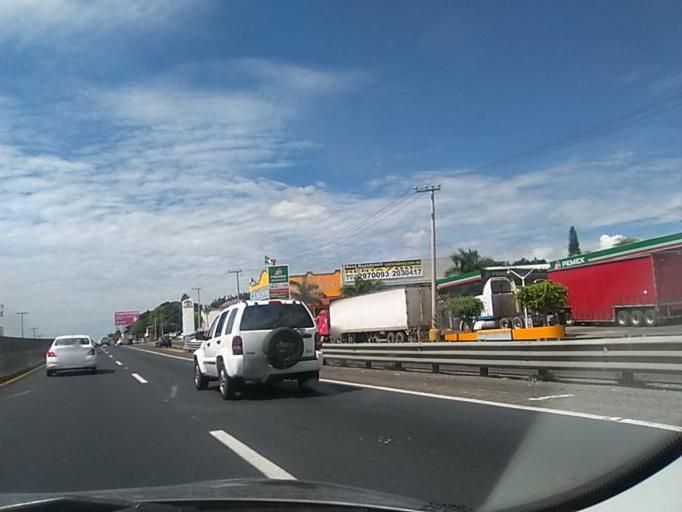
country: MX
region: Morelos
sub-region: Cuernavaca
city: Colonia los Cerritos
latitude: 18.9356
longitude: -99.1957
